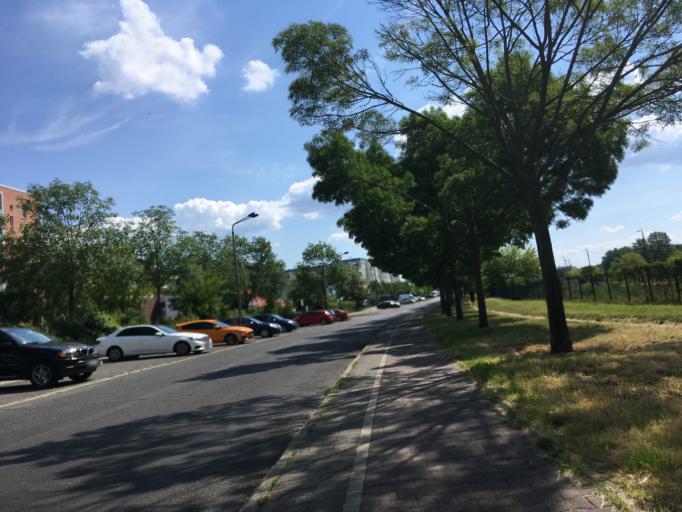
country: DE
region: Berlin
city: Hellersdorf
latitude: 52.5397
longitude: 13.6217
